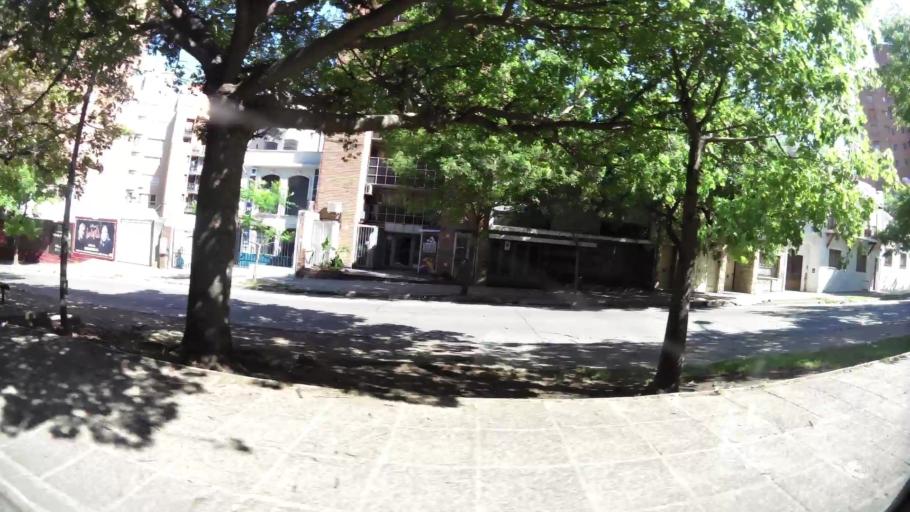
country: AR
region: Cordoba
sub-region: Departamento de Capital
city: Cordoba
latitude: -31.4305
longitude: -64.1890
